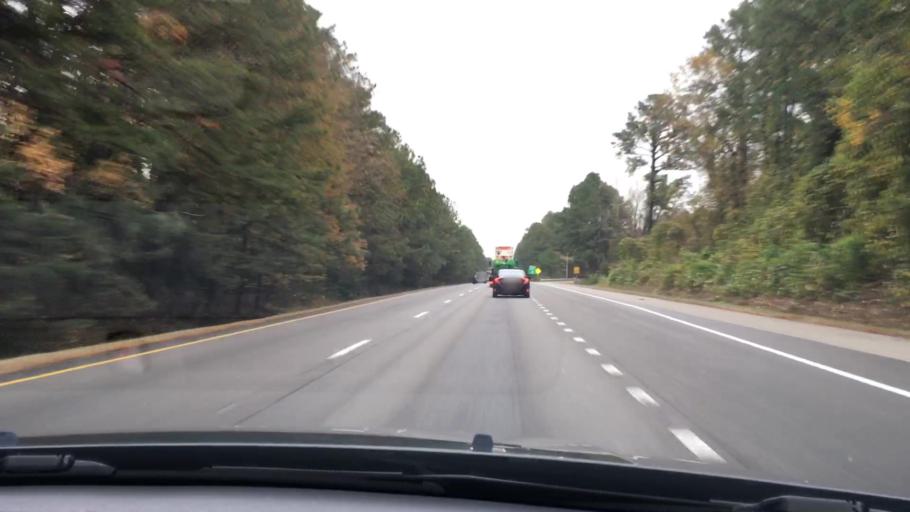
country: US
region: Virginia
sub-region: James City County
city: Williamsburg
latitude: 37.3562
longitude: -76.7357
